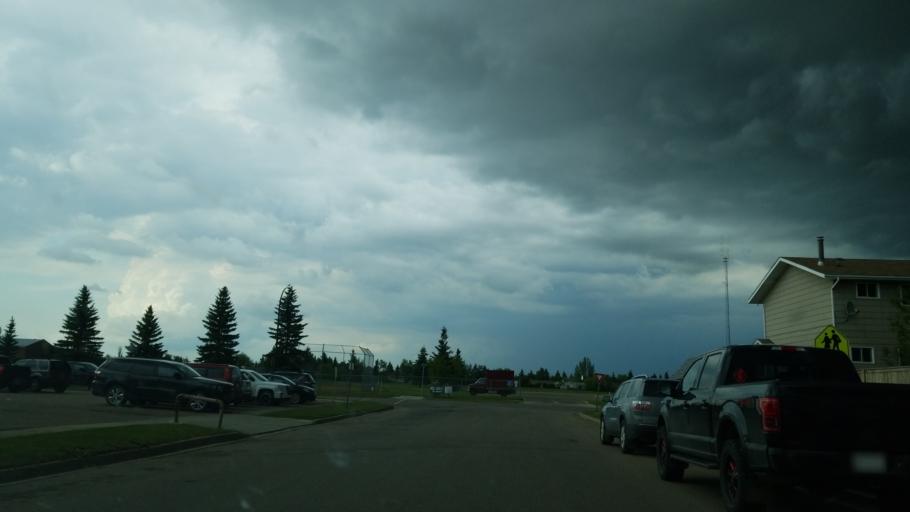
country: CA
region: Saskatchewan
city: Lloydminster
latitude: 53.2665
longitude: -110.0215
